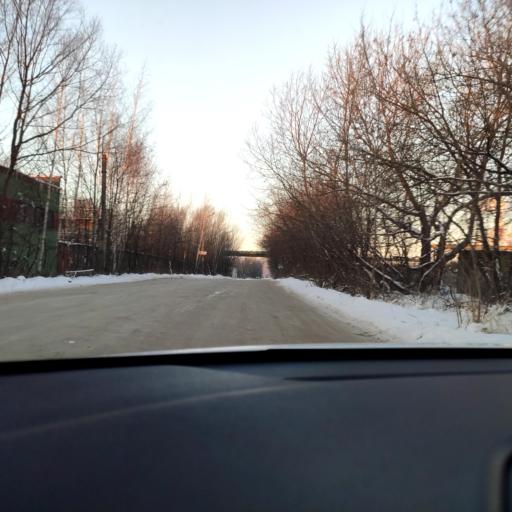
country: RU
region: Tatarstan
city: Staroye Arakchino
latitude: 55.8609
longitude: 48.9798
